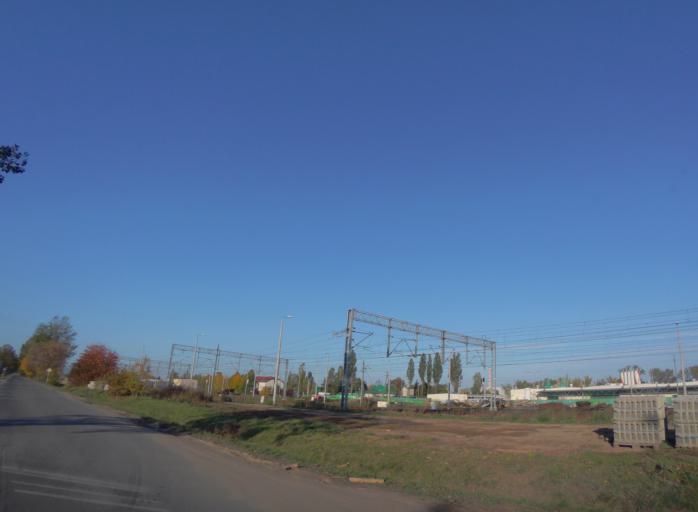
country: PL
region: Masovian Voivodeship
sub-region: Powiat pruszkowski
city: Pruszkow
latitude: 52.1614
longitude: 20.7789
